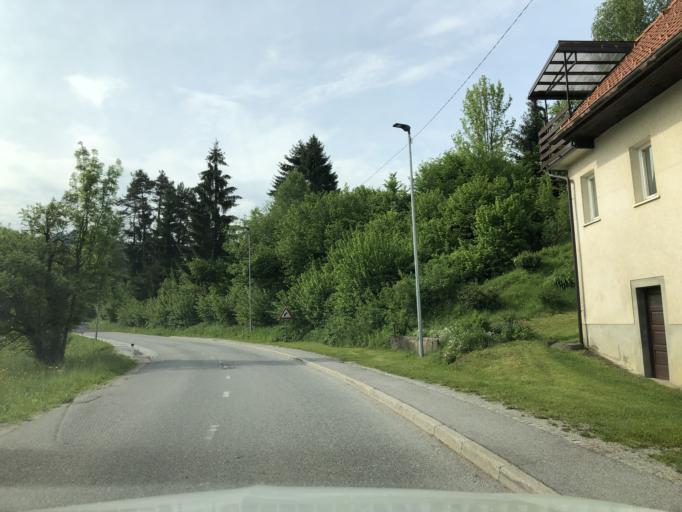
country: SI
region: Velike Lasce
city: Velike Lasce
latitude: 45.8305
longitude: 14.6359
